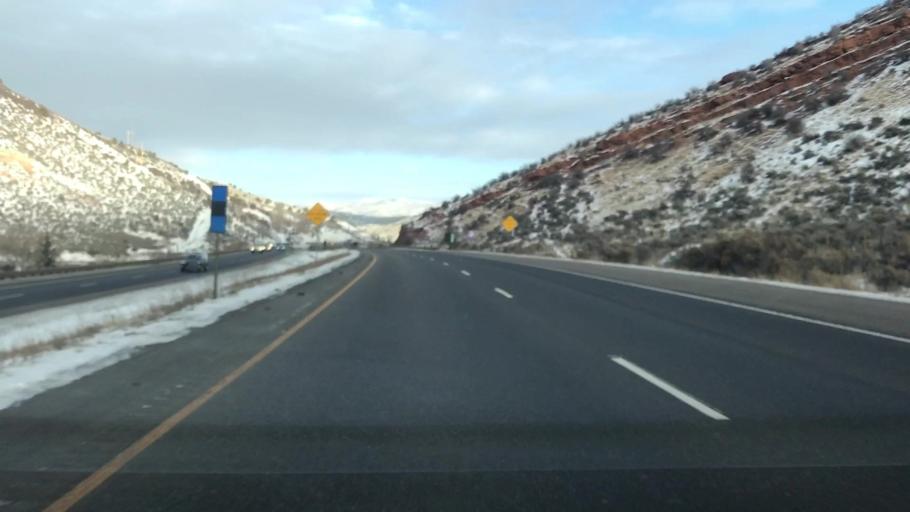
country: US
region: Colorado
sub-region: Eagle County
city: Edwards
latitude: 39.6705
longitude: -106.6451
